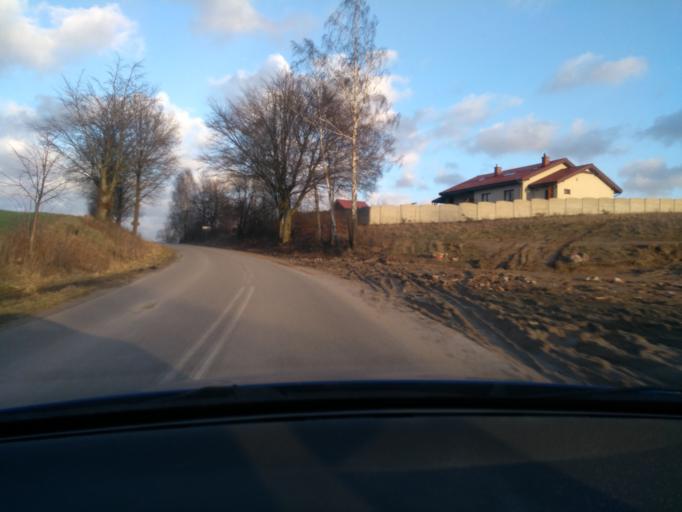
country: PL
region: Pomeranian Voivodeship
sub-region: Powiat kartuski
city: Przodkowo
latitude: 54.4158
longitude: 18.3038
